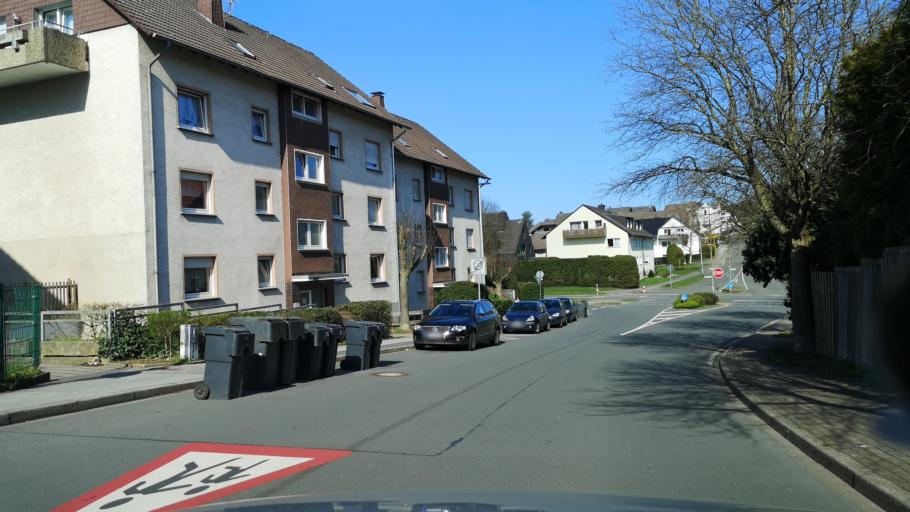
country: DE
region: North Rhine-Westphalia
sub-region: Regierungsbezirk Arnsberg
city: Menden
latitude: 51.4343
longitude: 7.7813
